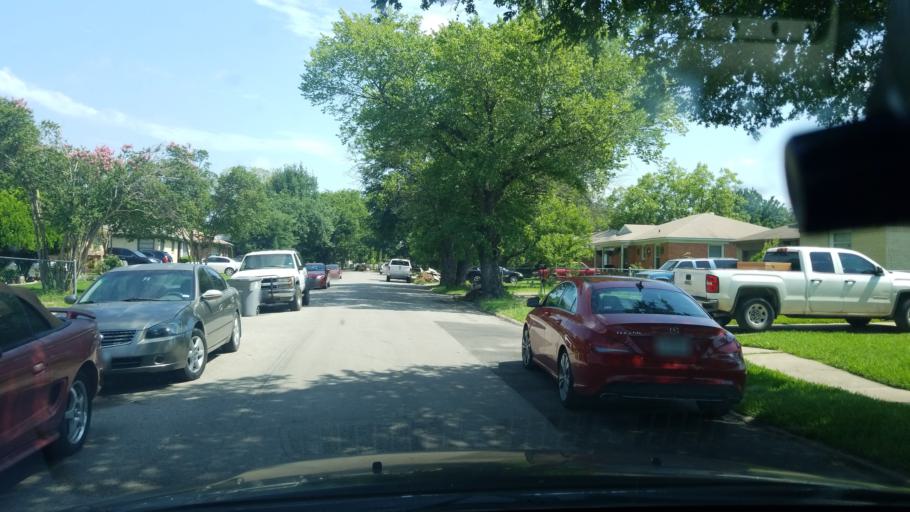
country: US
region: Texas
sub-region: Dallas County
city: Balch Springs
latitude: 32.7516
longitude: -96.6876
